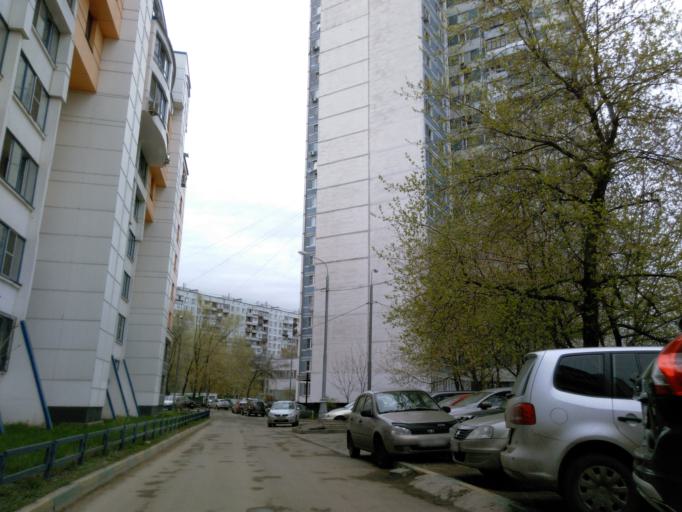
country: RU
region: Moskovskaya
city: Levoberezhnyy
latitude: 55.8530
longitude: 37.4499
